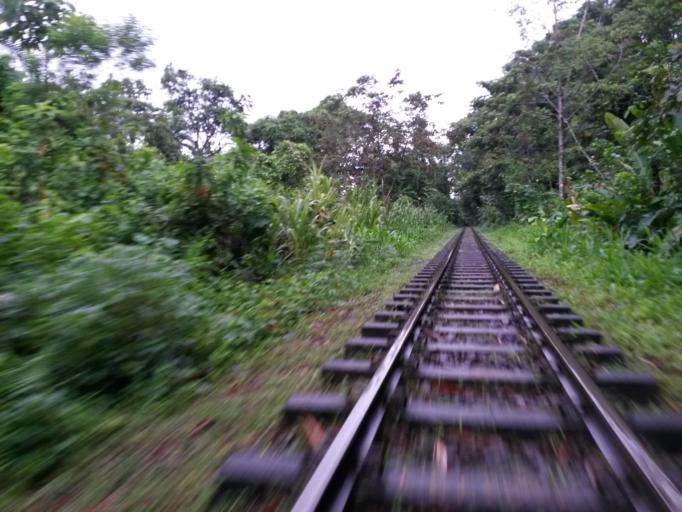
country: CO
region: Valle del Cauca
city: Buenaventura
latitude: 3.8431
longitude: -76.9056
